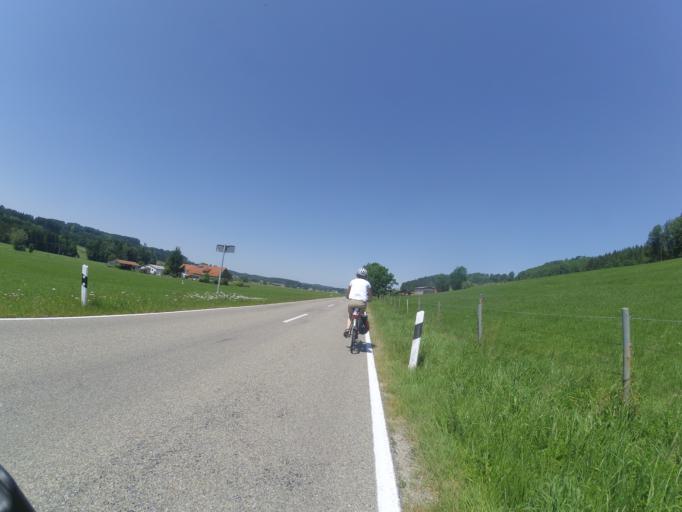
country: DE
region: Bavaria
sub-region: Swabia
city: Bohen
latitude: 47.8743
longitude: 10.3393
